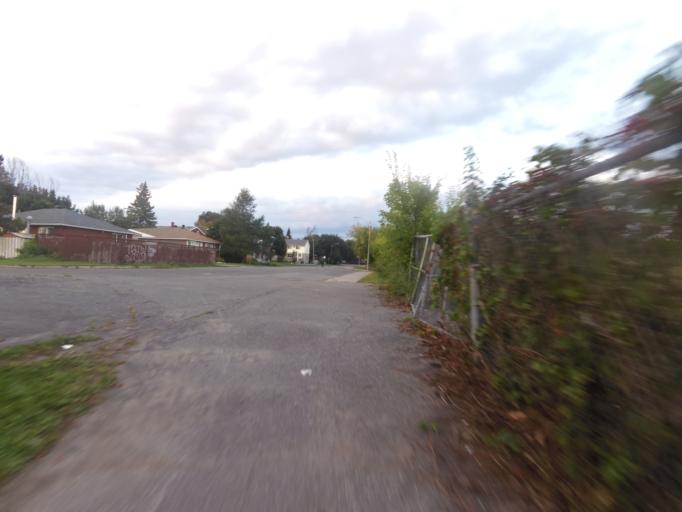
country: CA
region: Ontario
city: Ottawa
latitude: 45.4244
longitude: -75.6420
